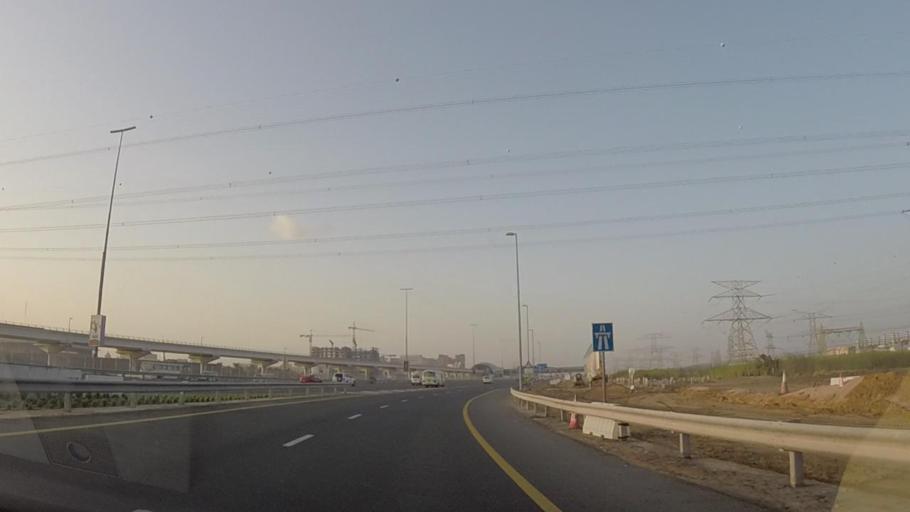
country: AE
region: Dubai
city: Dubai
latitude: 25.0461
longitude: 55.1162
